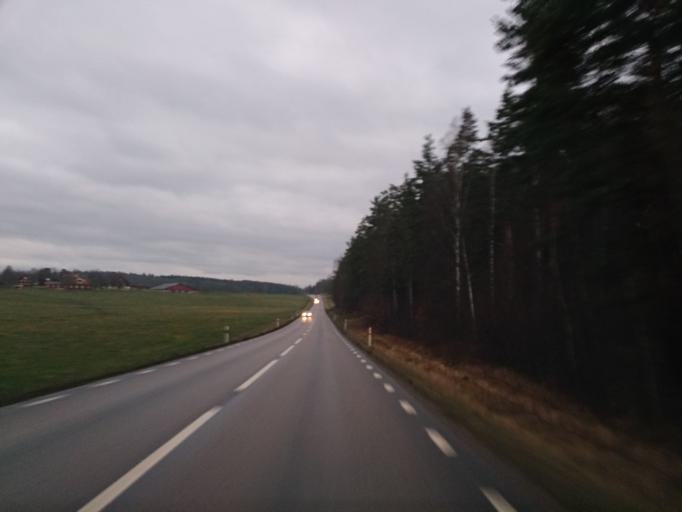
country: SE
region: OEstergoetland
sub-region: Atvidabergs Kommun
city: Atvidaberg
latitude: 58.2867
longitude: 15.8978
